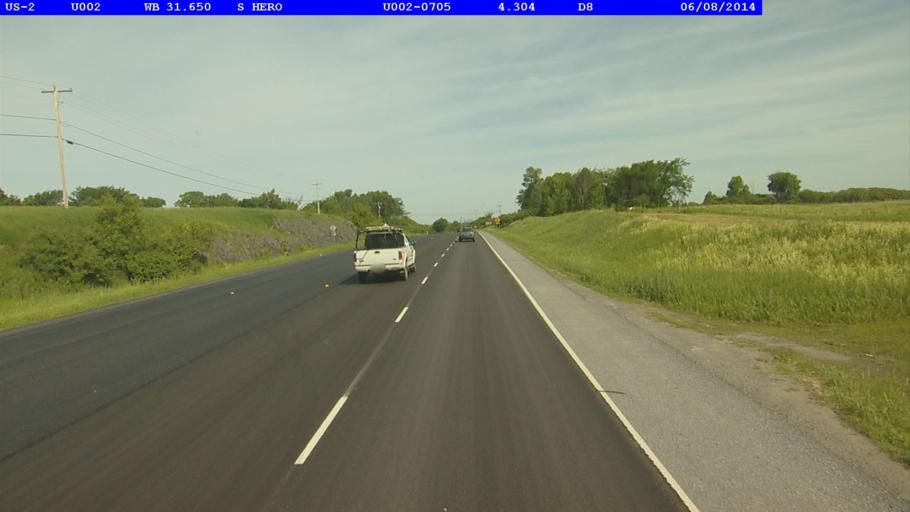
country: US
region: New York
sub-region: Clinton County
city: Cumberland Head
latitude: 44.6434
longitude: -73.2800
